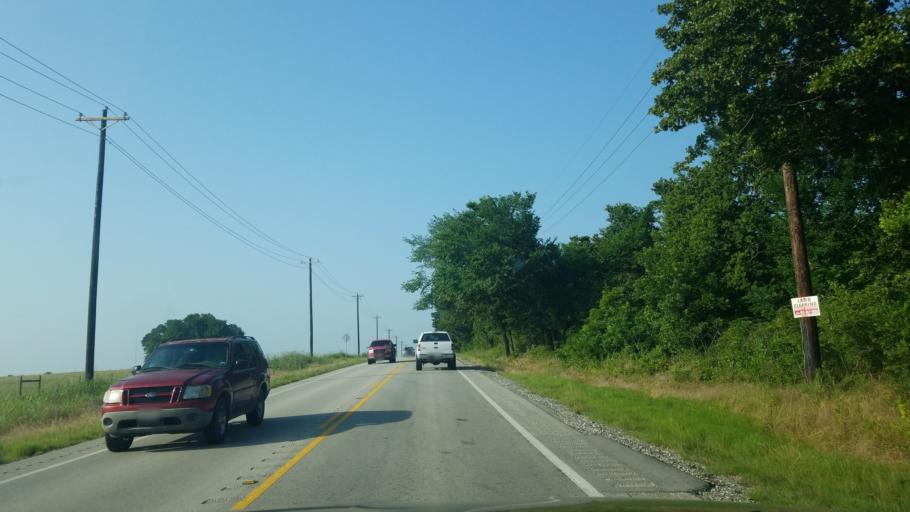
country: US
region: Texas
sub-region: Denton County
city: Aubrey
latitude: 33.3127
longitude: -96.9792
